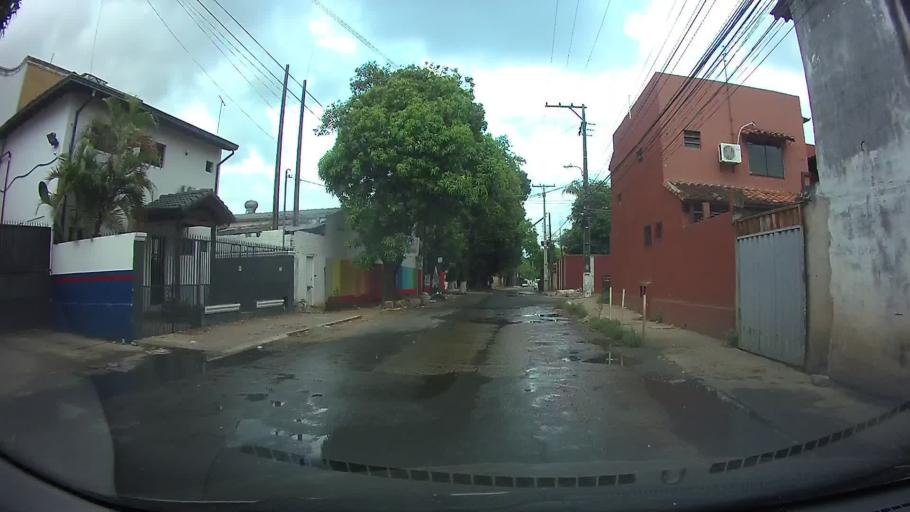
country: PY
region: Central
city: Fernando de la Mora
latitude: -25.3135
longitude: -57.5536
